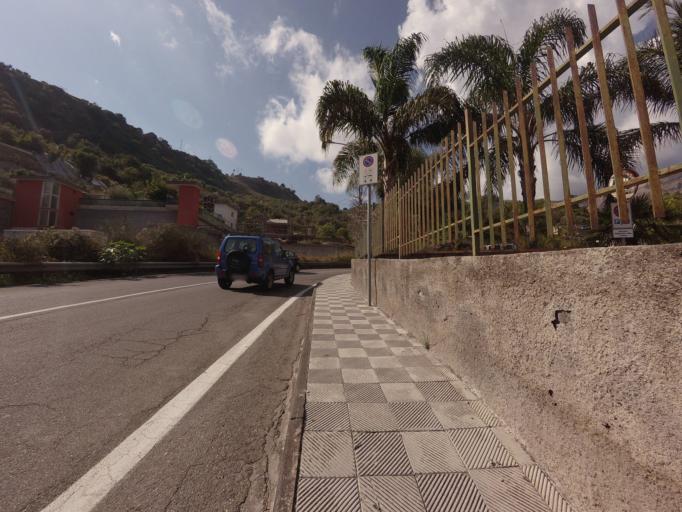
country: IT
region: Sicily
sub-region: Messina
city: Castelmola
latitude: 37.8460
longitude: 15.2773
